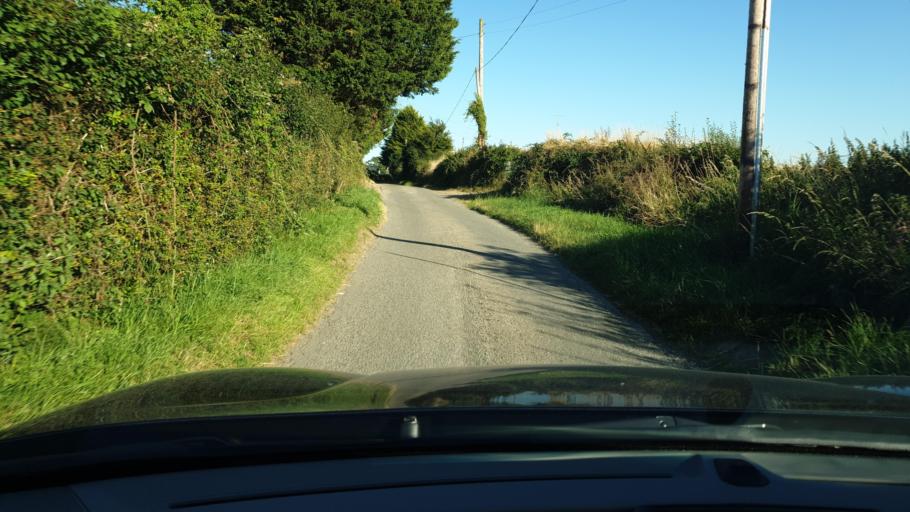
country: IE
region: Leinster
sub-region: Fingal County
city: Blanchardstown
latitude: 53.4369
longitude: -6.3589
